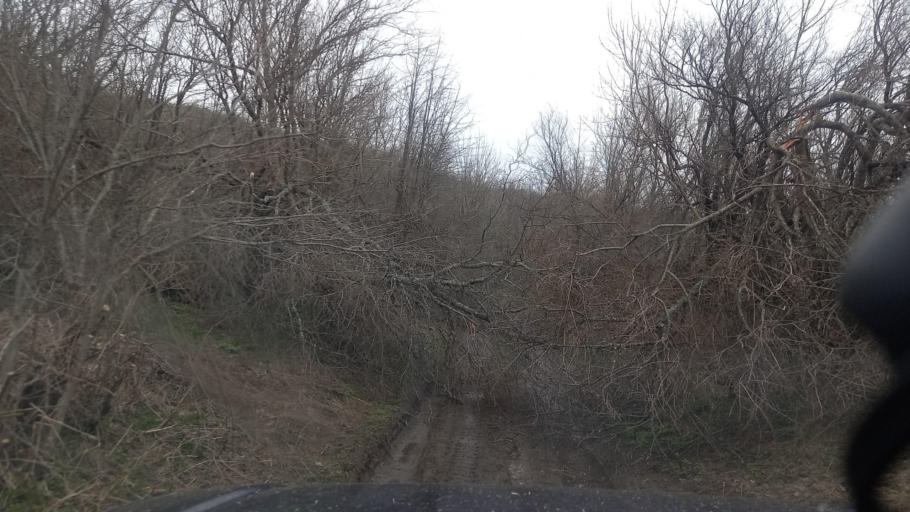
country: RU
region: Krasnodarskiy
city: Pshada
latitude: 44.5931
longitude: 38.2992
